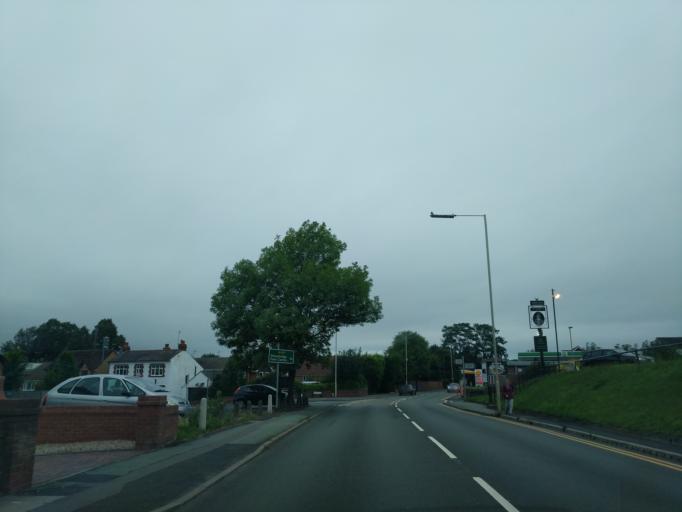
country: GB
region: England
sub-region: Dudley
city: Stourbridge
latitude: 52.4454
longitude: -2.1397
